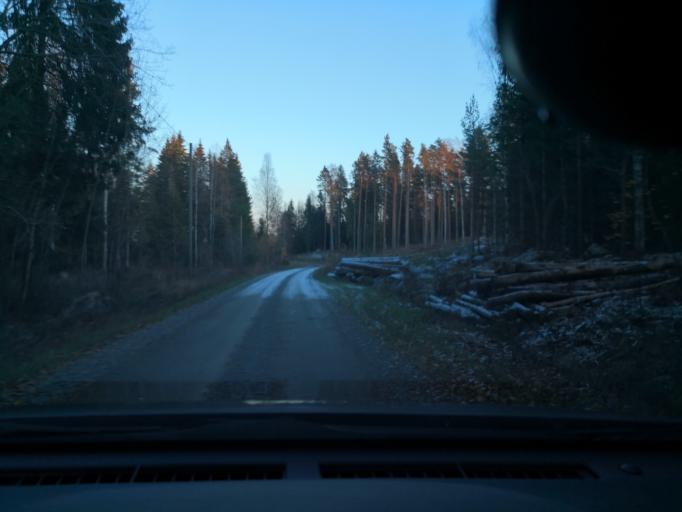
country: SE
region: Vaestmanland
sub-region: Vasteras
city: Tillberga
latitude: 59.7639
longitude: 16.6247
